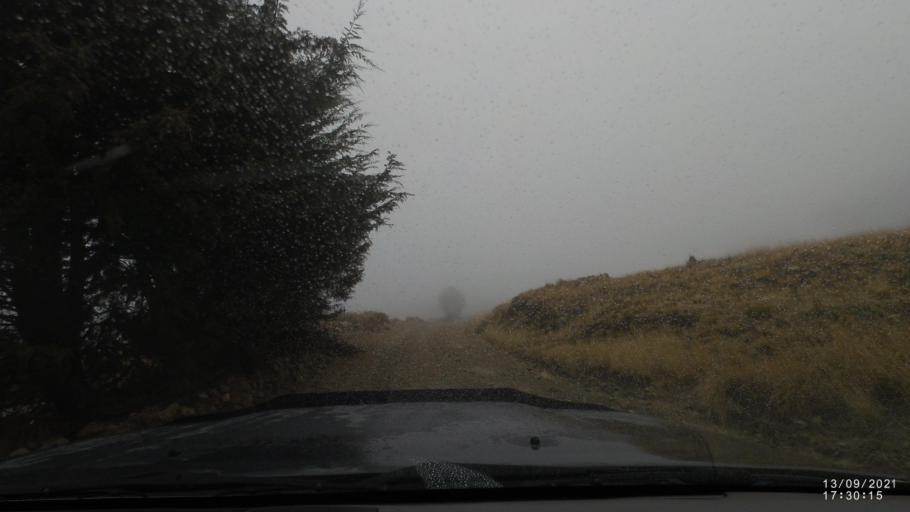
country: BO
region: Cochabamba
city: Colomi
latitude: -17.3619
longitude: -65.7856
